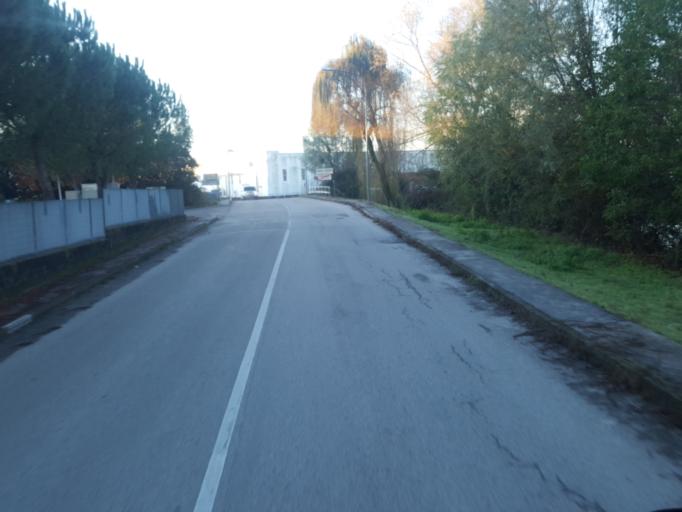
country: IT
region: Friuli Venezia Giulia
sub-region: Provincia di Pordenone
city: Orcenico Inferiore
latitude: 45.9490
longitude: 12.7725
